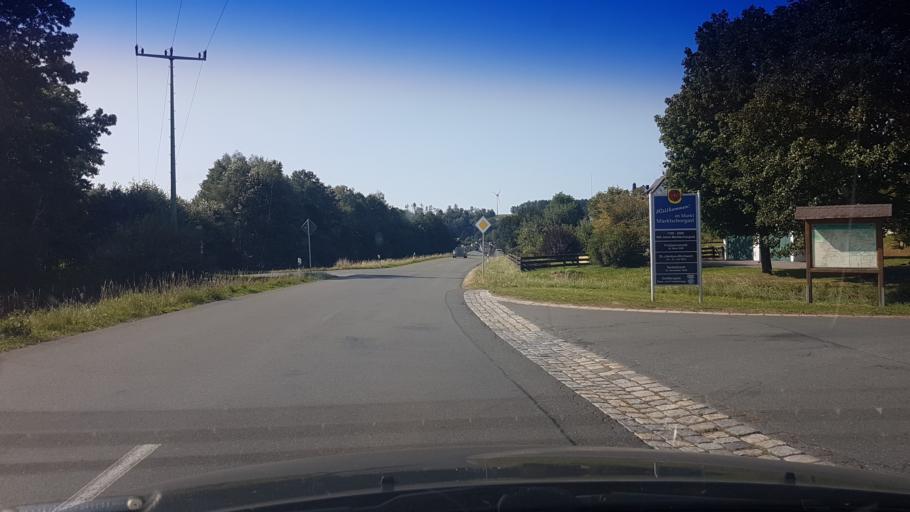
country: DE
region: Bavaria
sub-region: Upper Franconia
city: Marktschorgast
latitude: 50.0933
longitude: 11.6658
